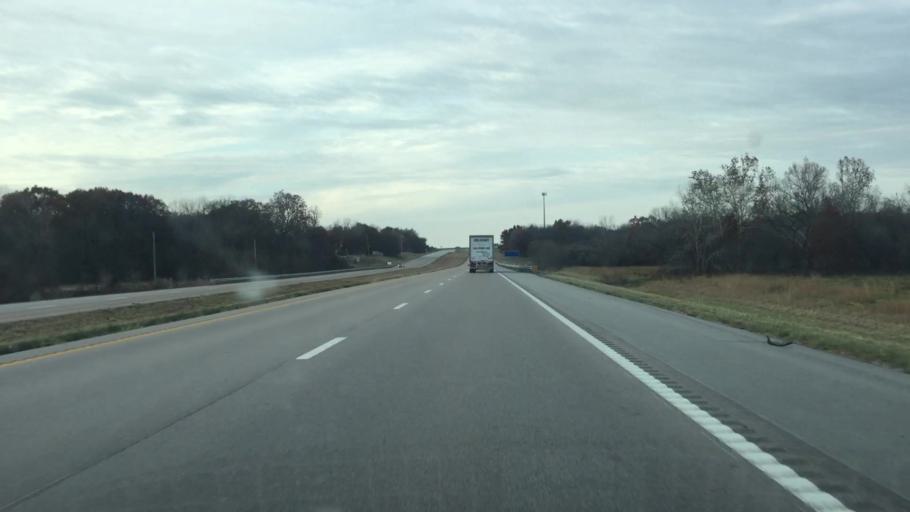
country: US
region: Missouri
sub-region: Cass County
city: Garden City
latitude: 38.4942
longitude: -94.0582
